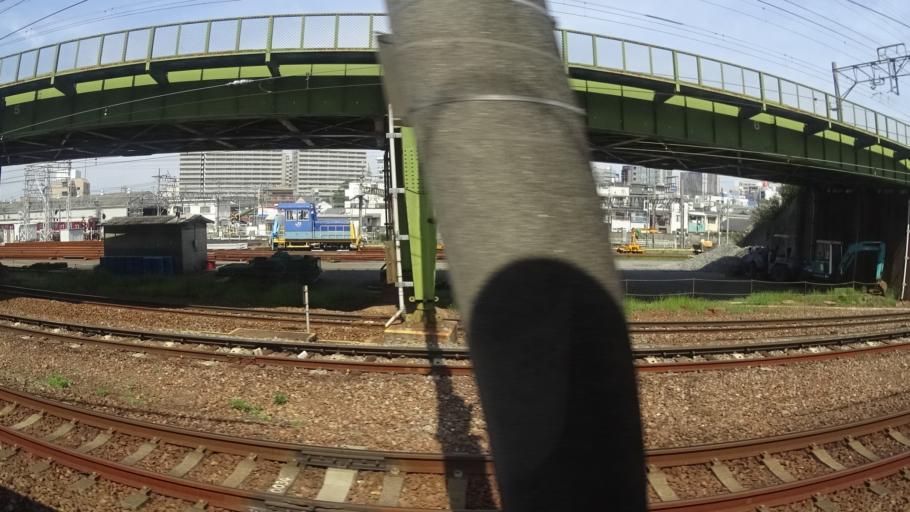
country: JP
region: Aichi
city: Nagoya-shi
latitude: 35.1636
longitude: 136.8835
